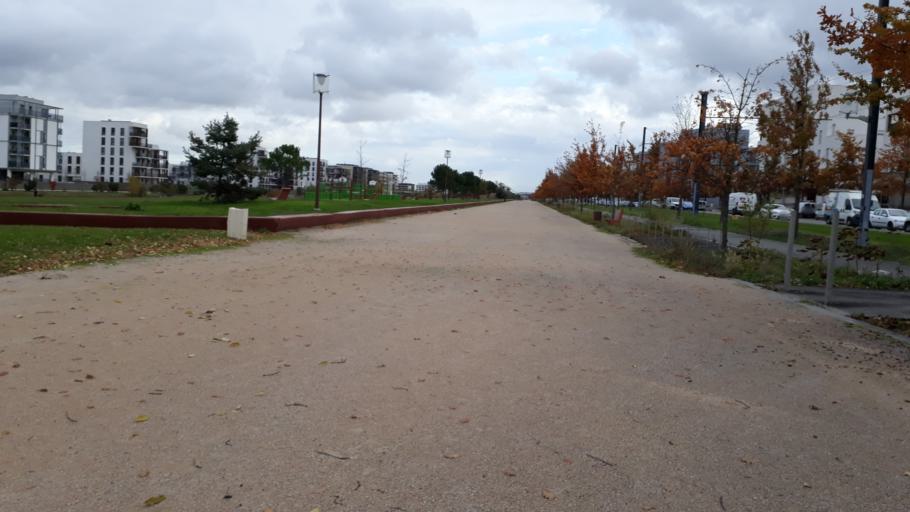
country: FR
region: Midi-Pyrenees
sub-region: Departement de la Haute-Garonne
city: Beauzelle
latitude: 43.6624
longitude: 1.3685
